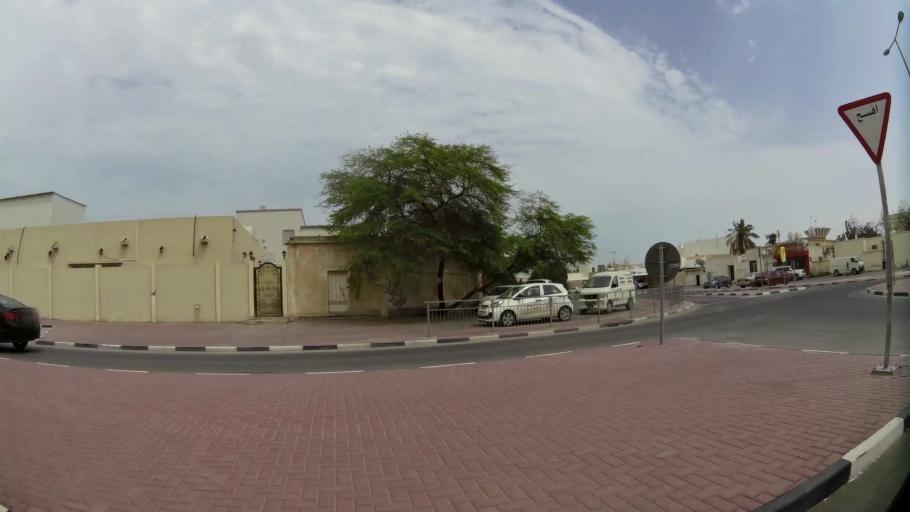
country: QA
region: Baladiyat ar Rayyan
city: Ar Rayyan
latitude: 25.3320
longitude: 51.4705
